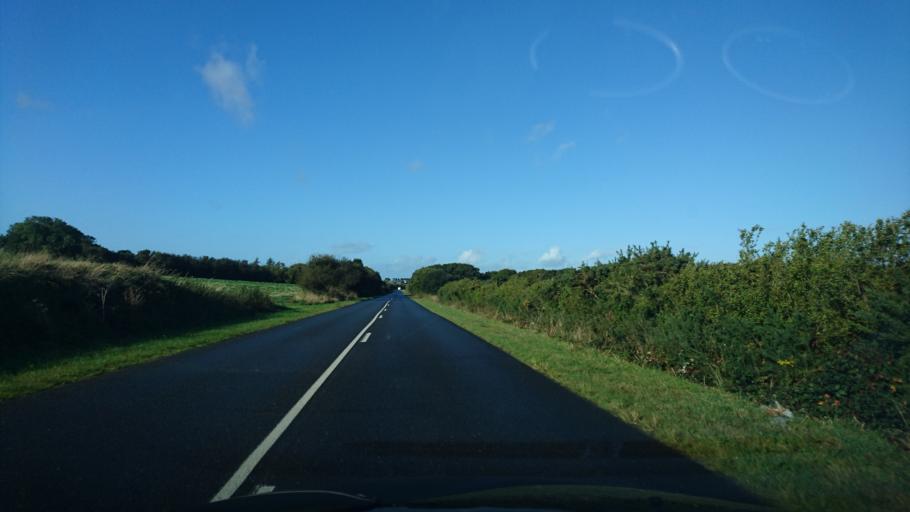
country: FR
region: Brittany
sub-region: Departement du Finistere
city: Plouarzel
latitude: 48.4386
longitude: -4.7205
